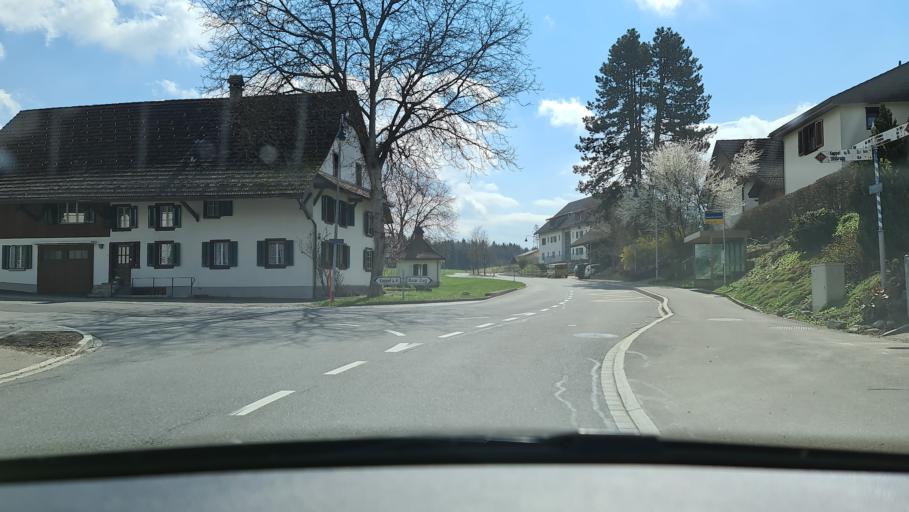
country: CH
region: Zug
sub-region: Zug
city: Steinhausen
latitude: 47.2222
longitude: 8.4992
